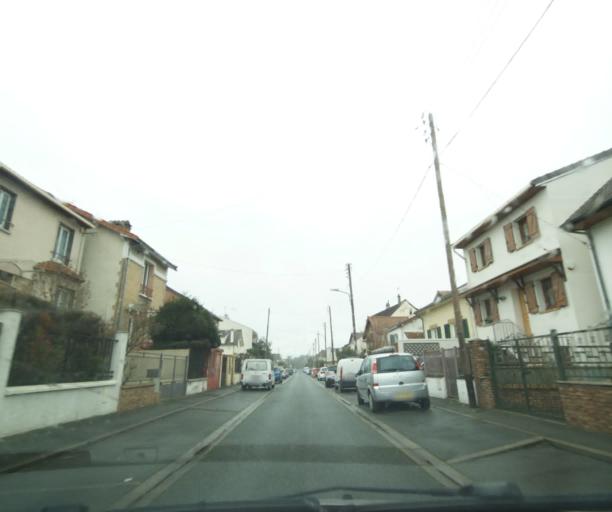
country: FR
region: Ile-de-France
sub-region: Departement du Val-de-Marne
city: Villeneuve-le-Roi
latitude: 48.7357
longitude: 2.4140
